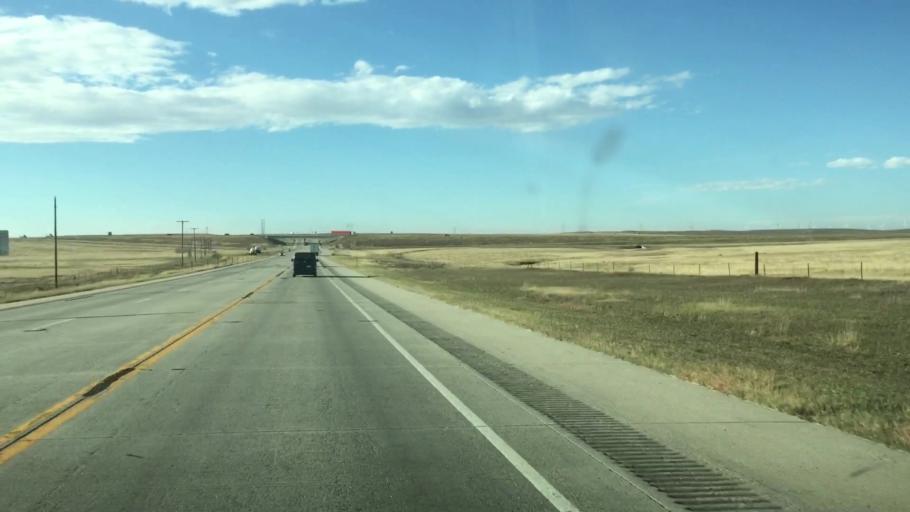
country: US
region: Colorado
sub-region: Lincoln County
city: Limon
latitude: 39.2572
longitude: -103.6411
